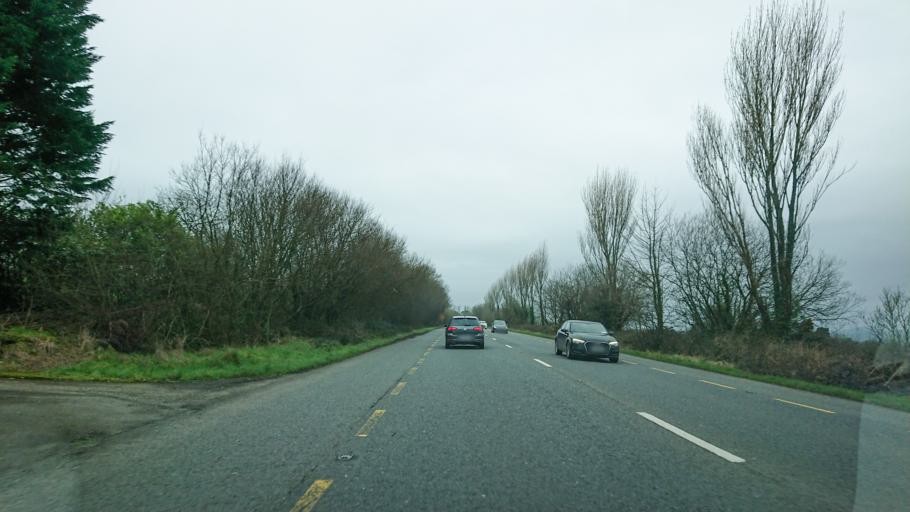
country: IE
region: Munster
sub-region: County Cork
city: Killumney
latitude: 51.7987
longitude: -8.5835
